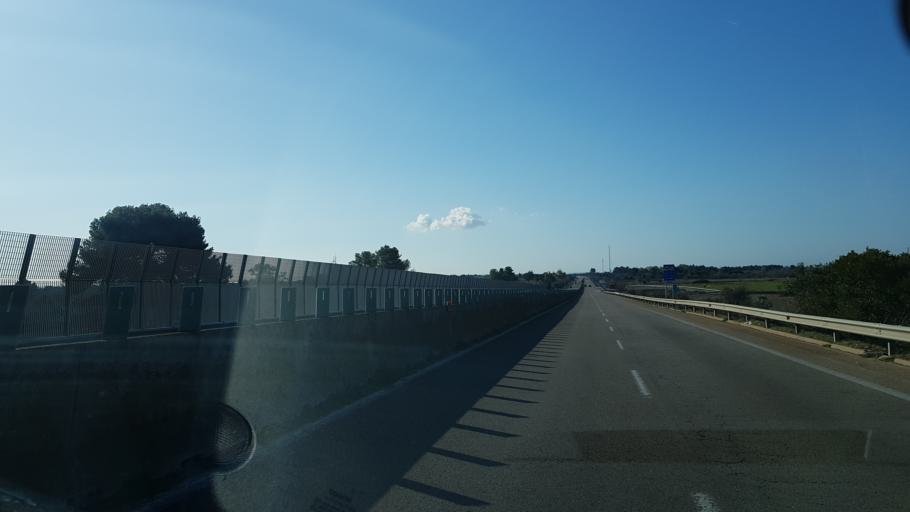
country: IT
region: Apulia
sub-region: Provincia di Lecce
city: Sannicola
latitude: 40.1106
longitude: 18.0394
